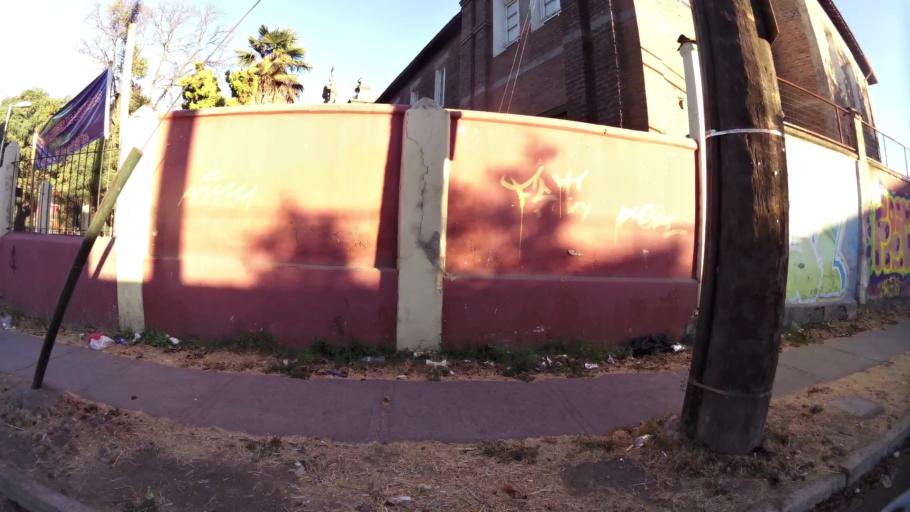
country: CL
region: O'Higgins
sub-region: Provincia de Cachapoal
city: Rancagua
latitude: -34.1683
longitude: -70.7555
